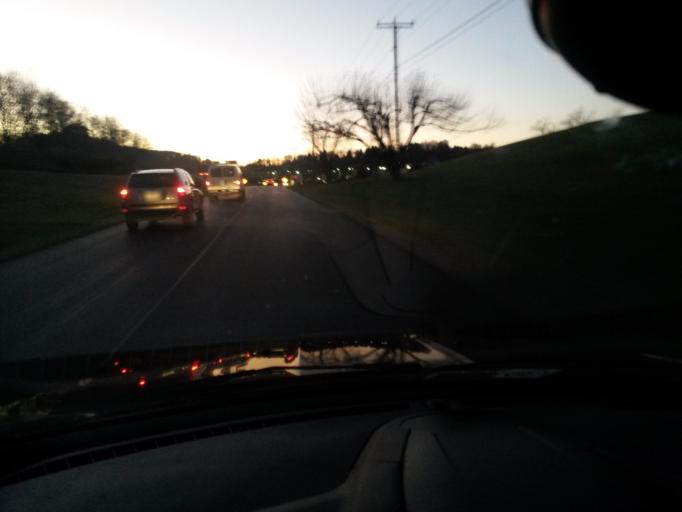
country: US
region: Virginia
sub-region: Botetourt County
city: Daleville
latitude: 37.3999
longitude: -79.9111
